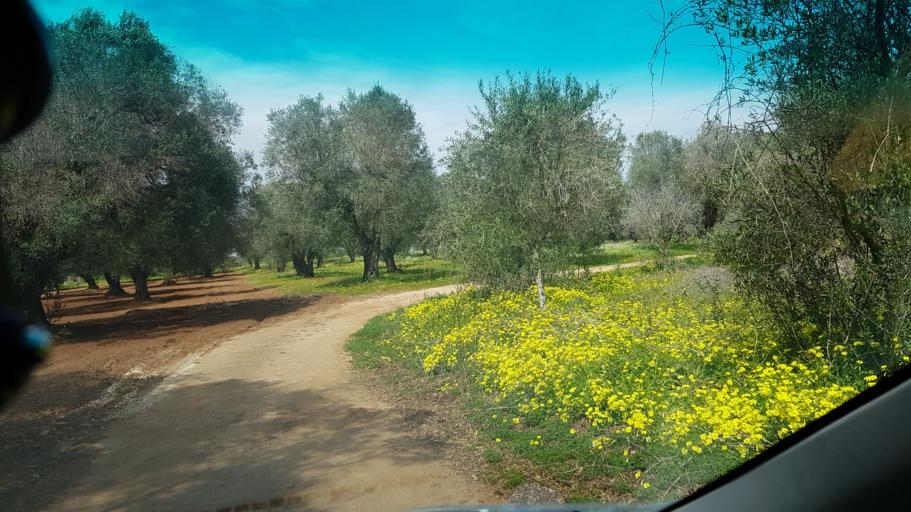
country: IT
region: Apulia
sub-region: Provincia di Brindisi
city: Mesagne
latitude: 40.6077
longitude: 17.8522
